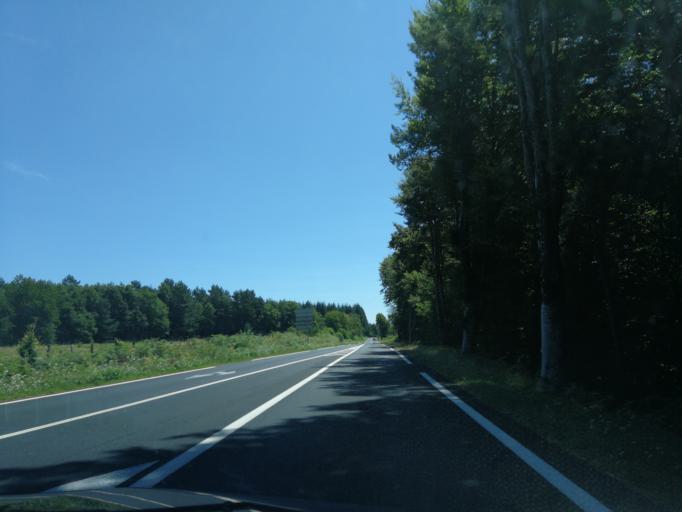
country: FR
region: Limousin
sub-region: Departement de la Correze
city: Saint-Privat
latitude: 45.0041
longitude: 2.0500
